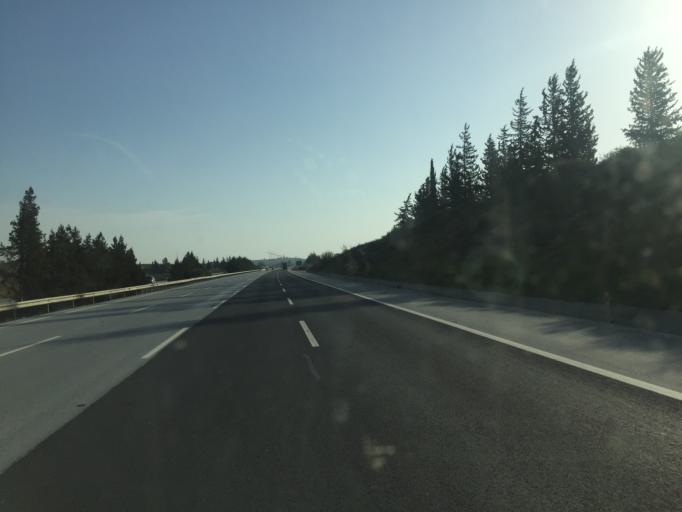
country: TR
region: Mersin
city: Yenice
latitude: 37.0228
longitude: 35.0503
